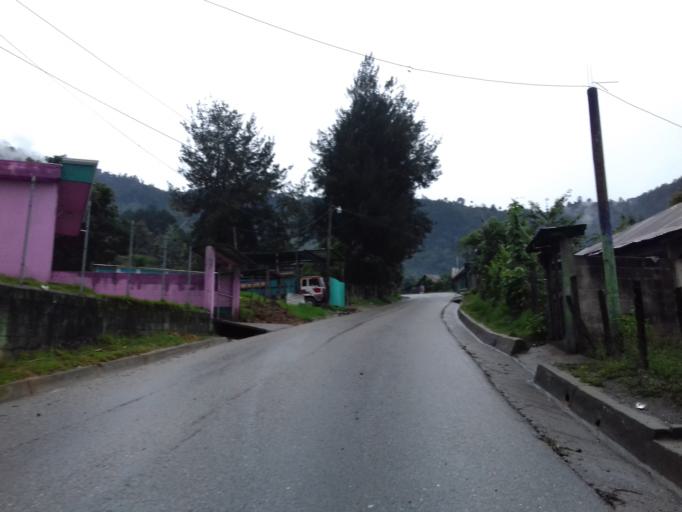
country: GT
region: Quiche
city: Nebaj
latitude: 15.3846
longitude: -91.1117
